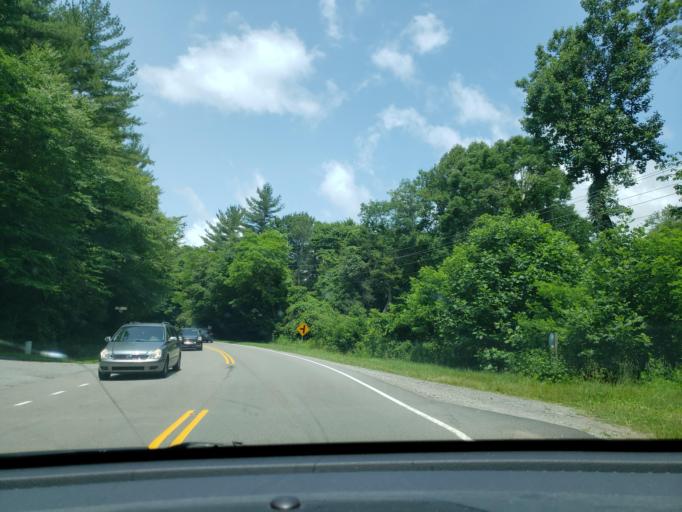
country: US
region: North Carolina
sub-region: Watauga County
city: Blowing Rock
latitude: 36.1396
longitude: -81.6898
